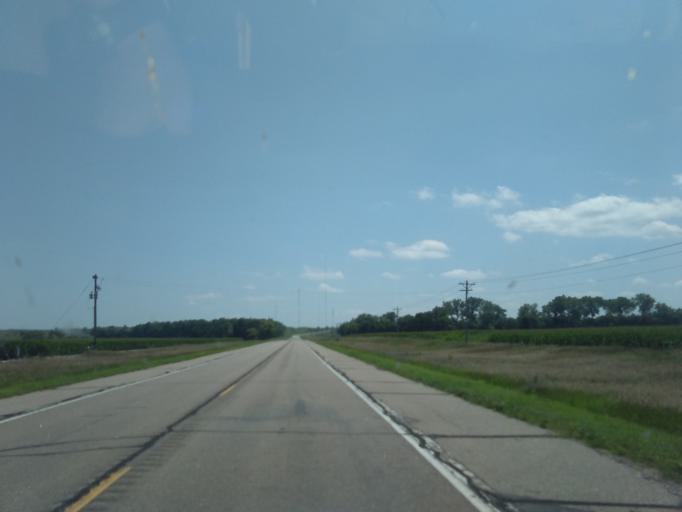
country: US
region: Nebraska
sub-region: Dawson County
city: Lexington
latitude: 40.7182
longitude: -99.7874
